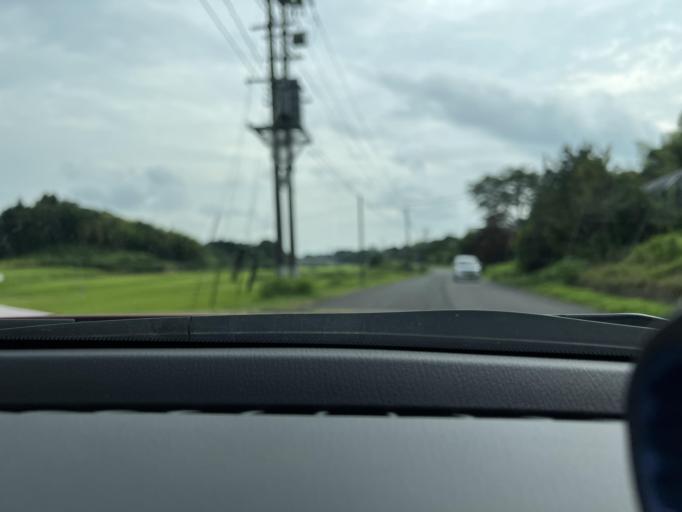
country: JP
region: Fukushima
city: Motomiya
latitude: 37.5249
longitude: 140.4335
